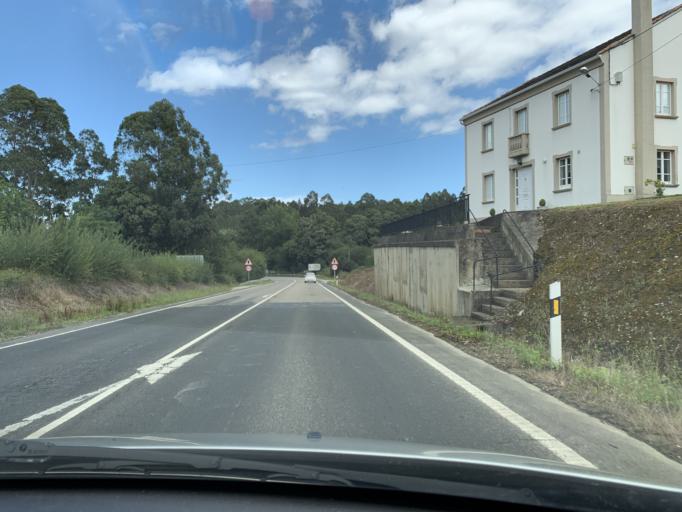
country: ES
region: Galicia
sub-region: Provincia de Lugo
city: Barreiros
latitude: 43.5313
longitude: -7.2627
